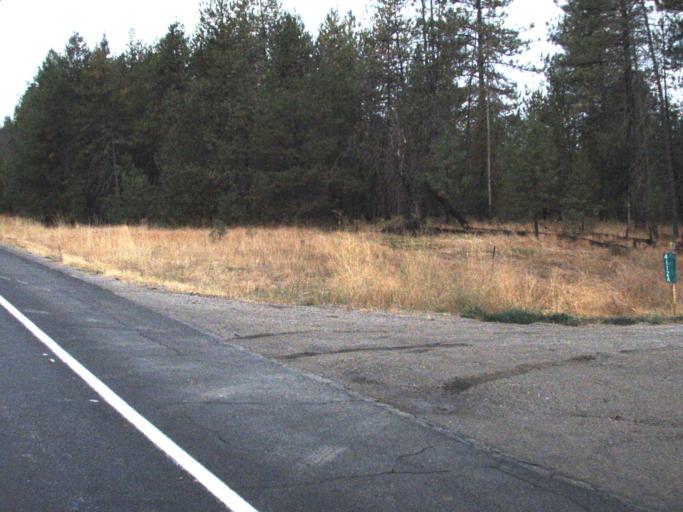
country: US
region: Washington
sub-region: Spokane County
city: Deer Park
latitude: 48.0642
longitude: -117.6572
